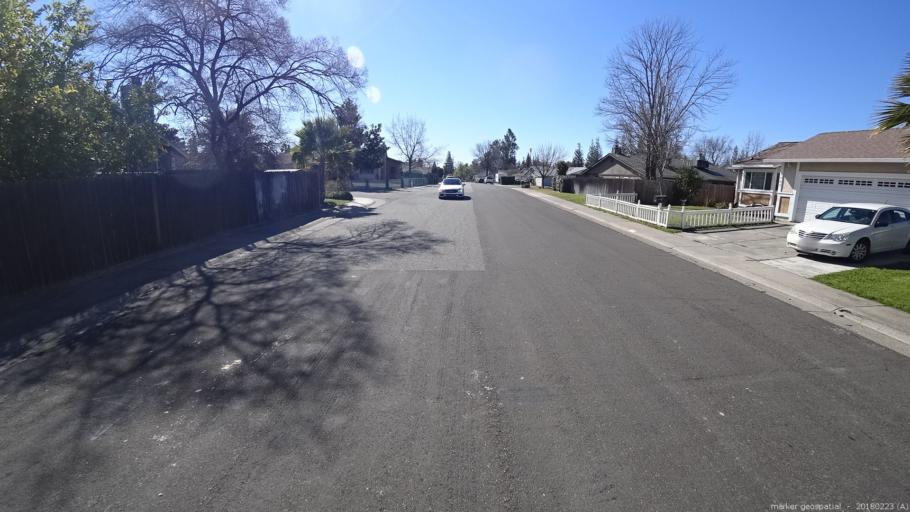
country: US
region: California
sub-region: Sacramento County
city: North Highlands
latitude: 38.7072
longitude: -121.3799
